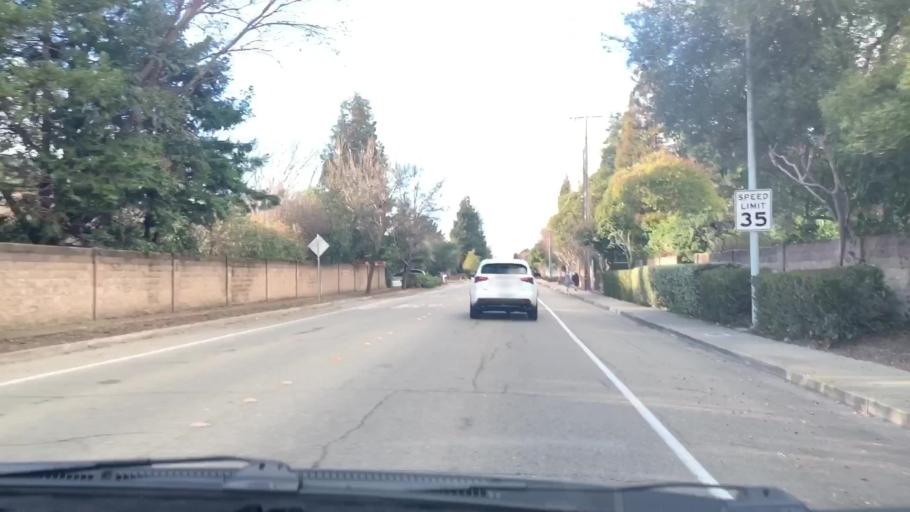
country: US
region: California
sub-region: Contra Costa County
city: San Ramon
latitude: 37.7875
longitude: -121.9785
